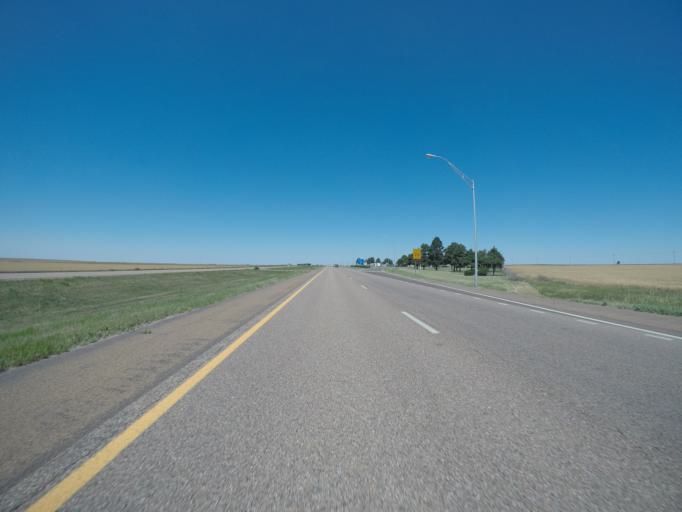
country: US
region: Kansas
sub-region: Trego County
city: WaKeeney
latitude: 38.9952
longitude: -99.7860
